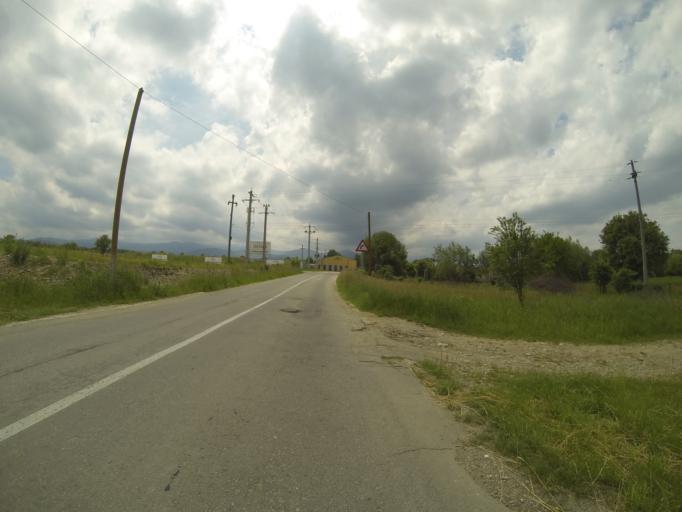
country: RO
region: Brasov
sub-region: Comuna Sinca Veche
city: Sinca Veche
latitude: 45.7498
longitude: 25.1285
